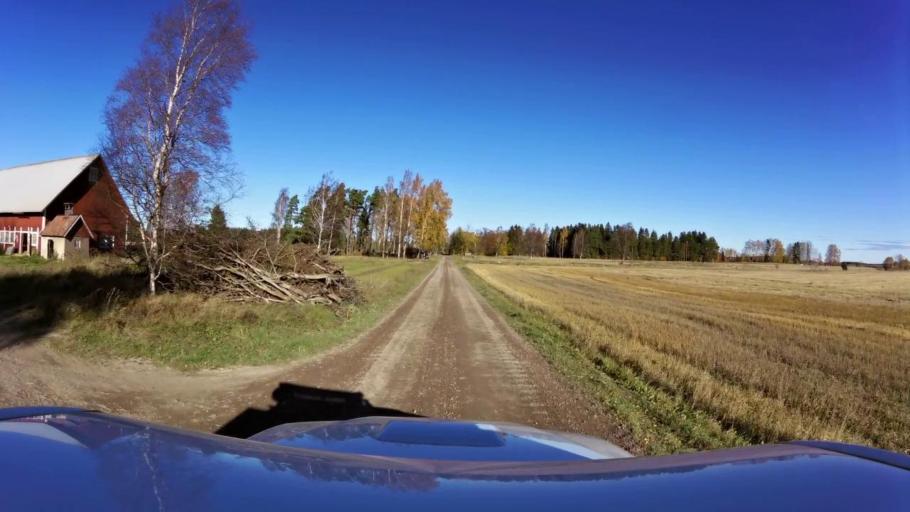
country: SE
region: OEstergoetland
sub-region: Linkopings Kommun
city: Ljungsbro
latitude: 58.5004
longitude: 15.3858
